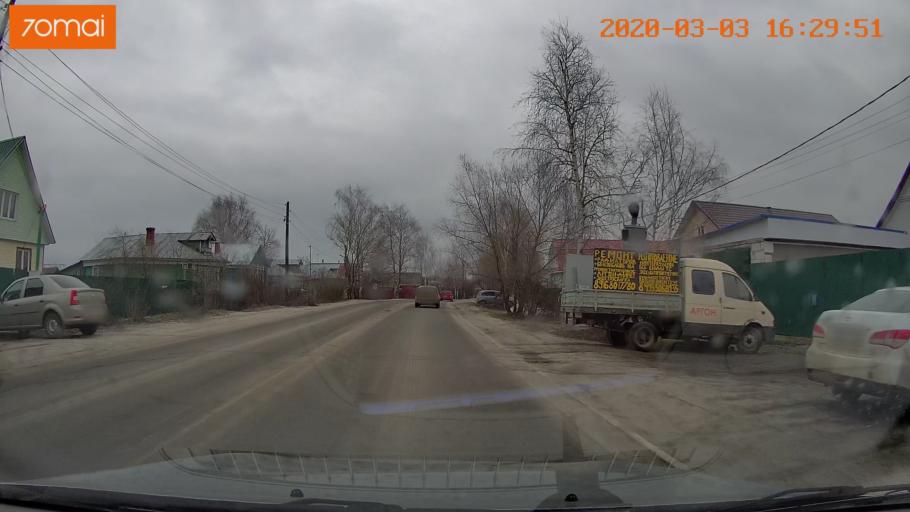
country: RU
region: Moskovskaya
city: Konobeyevo
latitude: 55.4356
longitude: 38.7056
